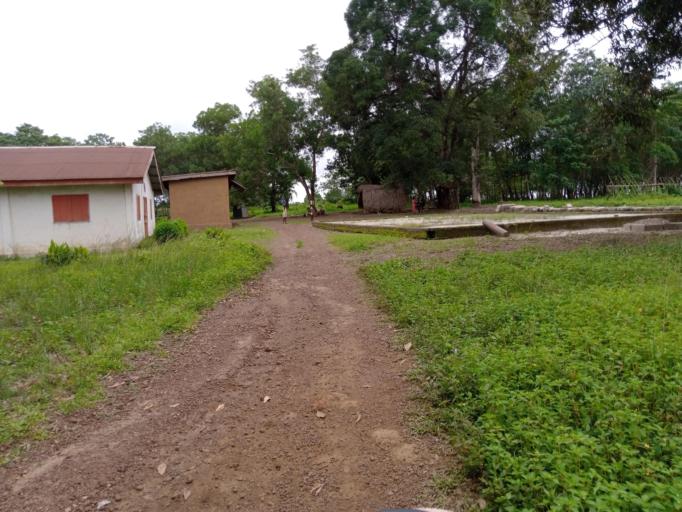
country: SL
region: Southern Province
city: Moyamba
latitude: 8.1554
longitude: -12.4177
